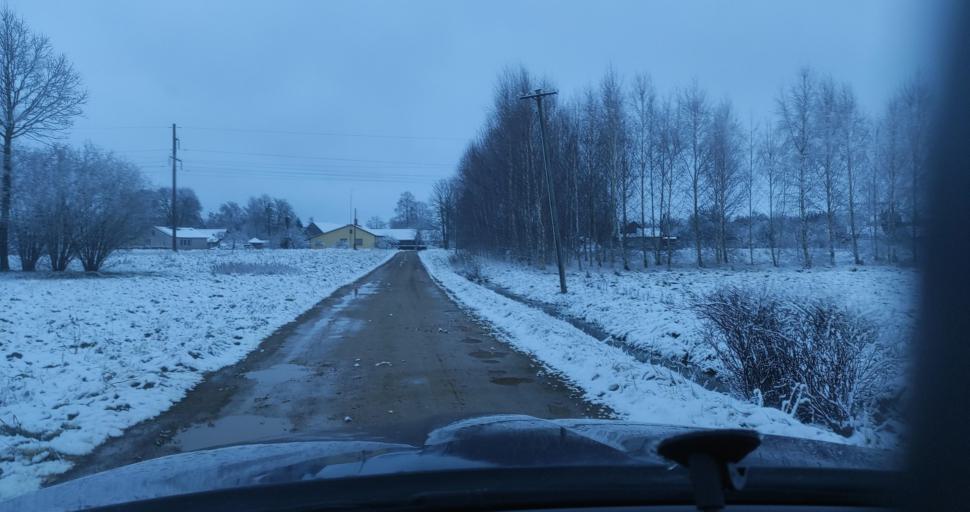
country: LV
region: Skrunda
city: Skrunda
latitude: 56.8705
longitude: 22.2302
